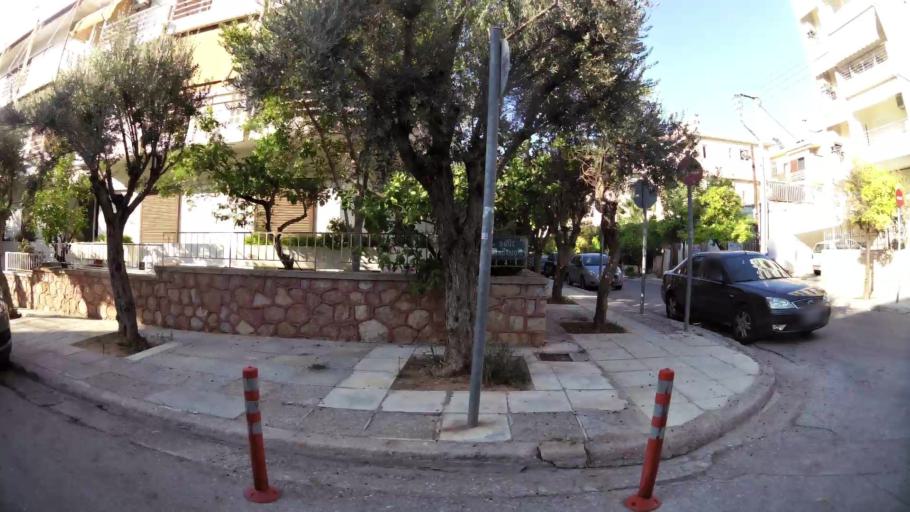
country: GR
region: Attica
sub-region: Nomarchia Athinas
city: Argyroupoli
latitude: 37.8984
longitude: 23.7483
